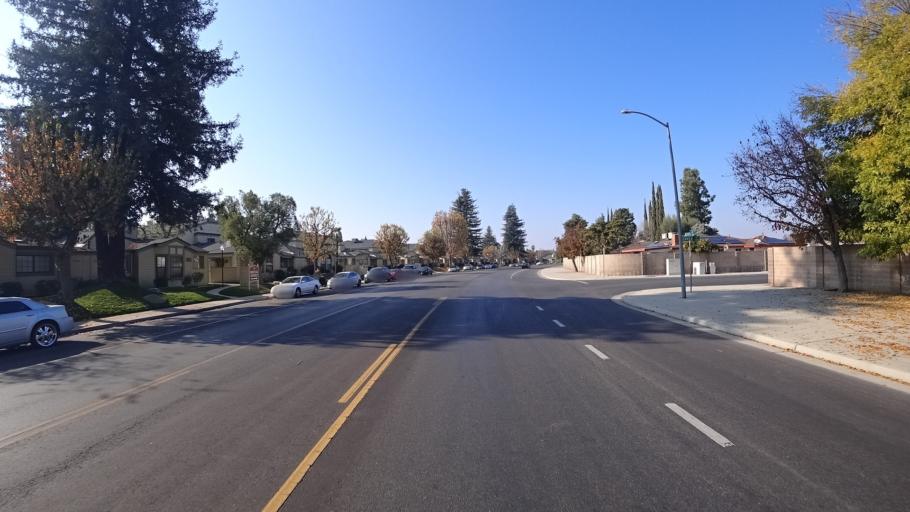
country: US
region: California
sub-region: Kern County
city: Greenacres
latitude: 35.3229
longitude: -119.0843
